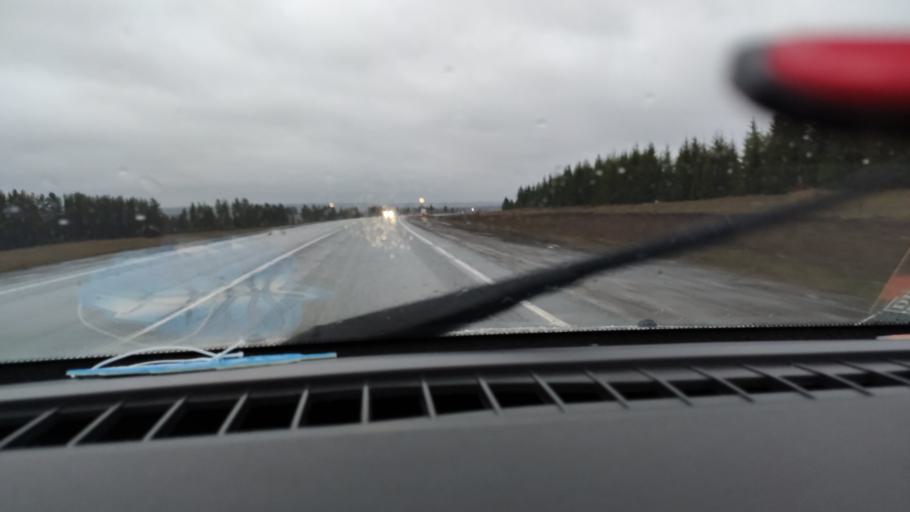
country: RU
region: Tatarstan
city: Mendeleyevsk
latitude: 56.0400
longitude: 52.3874
